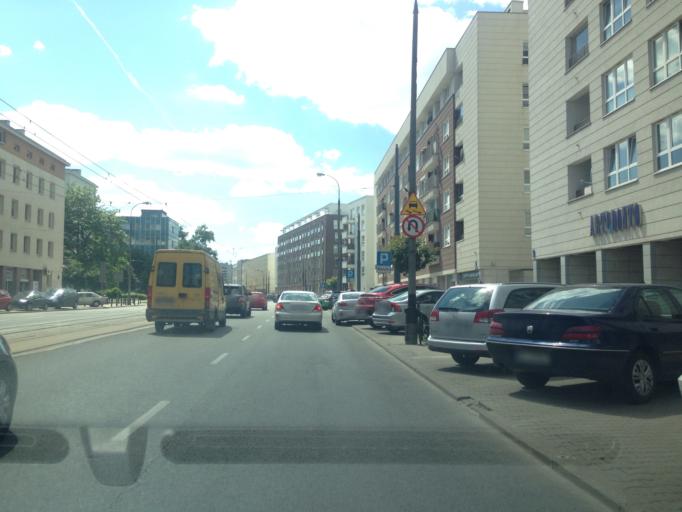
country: PL
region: Masovian Voivodeship
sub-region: Warszawa
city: Wola
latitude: 52.2540
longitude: 20.9934
